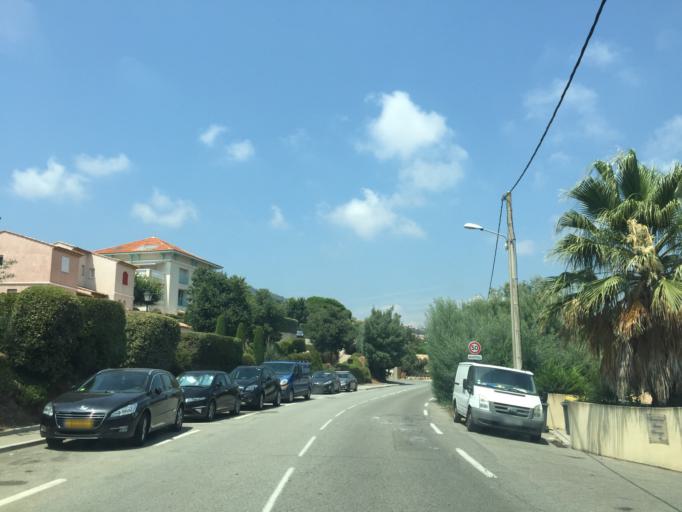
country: FR
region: Provence-Alpes-Cote d'Azur
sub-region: Departement du Var
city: Sainte-Maxime
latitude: 43.3422
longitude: 6.6795
